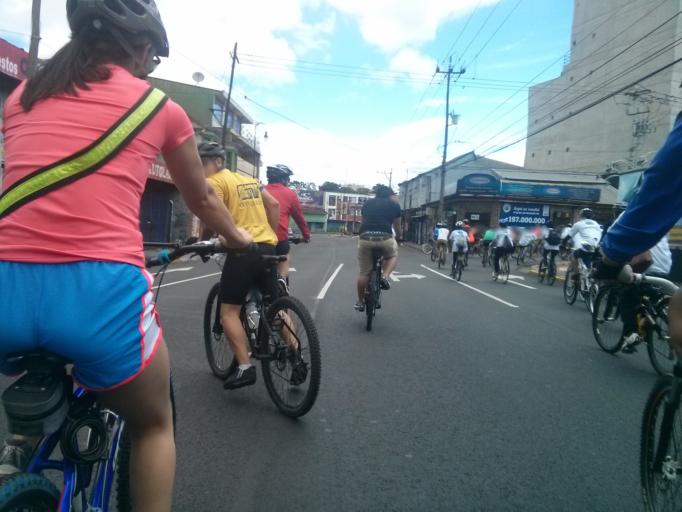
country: CR
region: San Jose
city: San Jose
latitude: 9.9325
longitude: -84.0682
